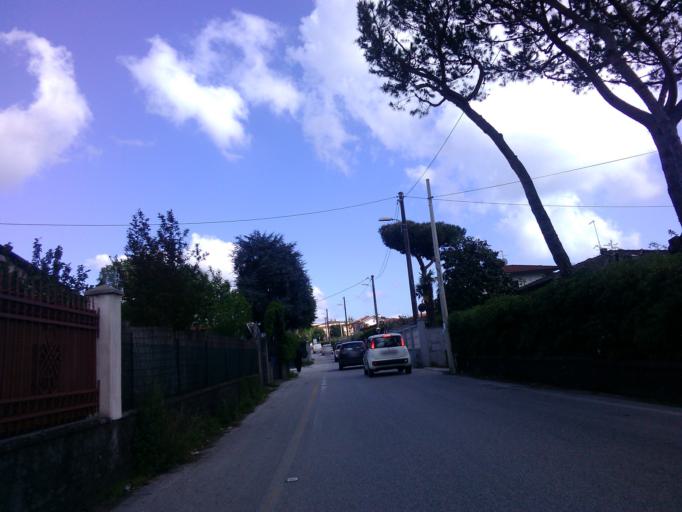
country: IT
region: Tuscany
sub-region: Provincia di Massa-Carrara
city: Massa
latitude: 44.0222
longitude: 10.1226
